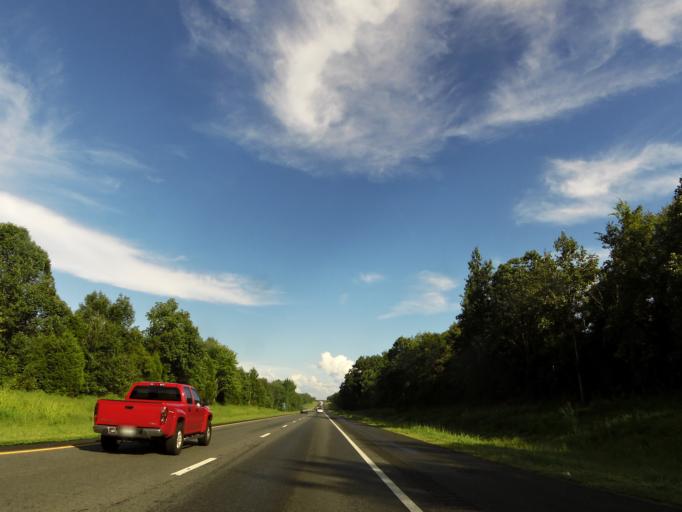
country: US
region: Tennessee
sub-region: Cheatham County
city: Pleasant View
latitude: 36.4840
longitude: -87.1553
